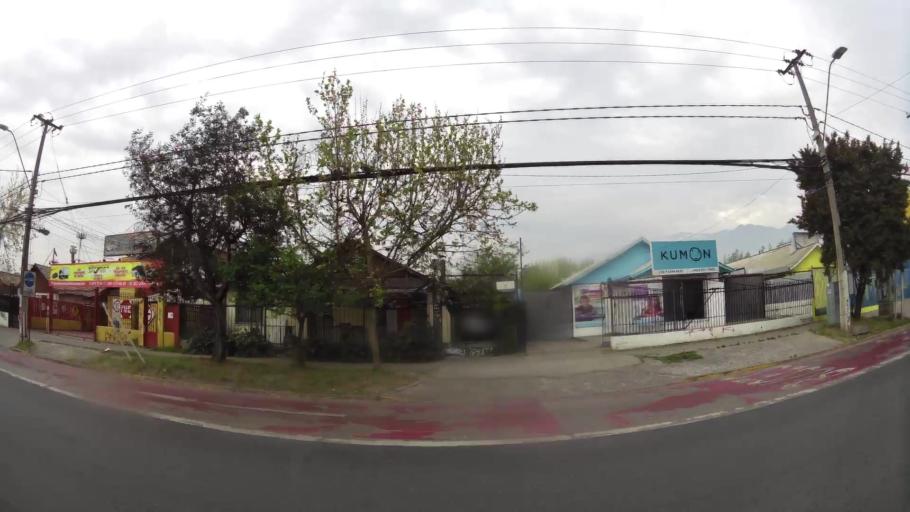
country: CL
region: Santiago Metropolitan
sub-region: Provincia de Santiago
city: Villa Presidente Frei, Nunoa, Santiago, Chile
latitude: -33.4964
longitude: -70.5983
